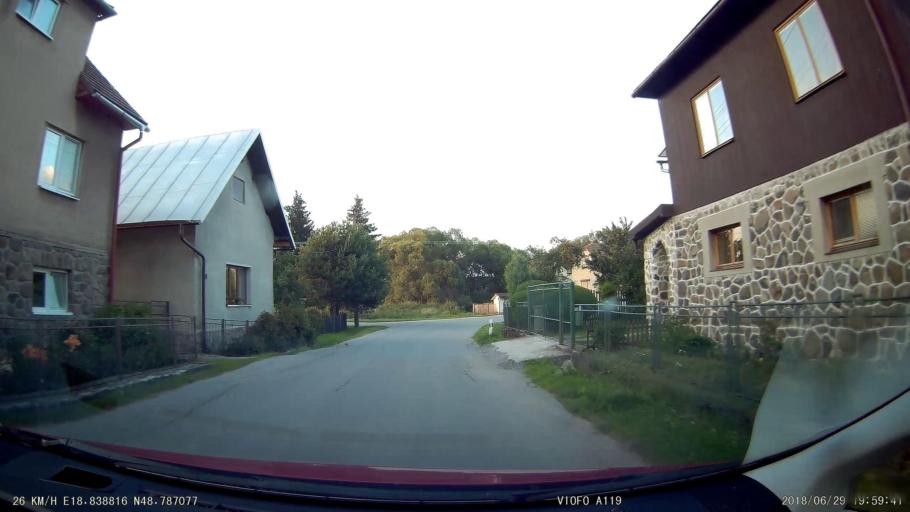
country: SK
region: Nitriansky
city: Handlova
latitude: 48.7871
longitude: 18.8389
